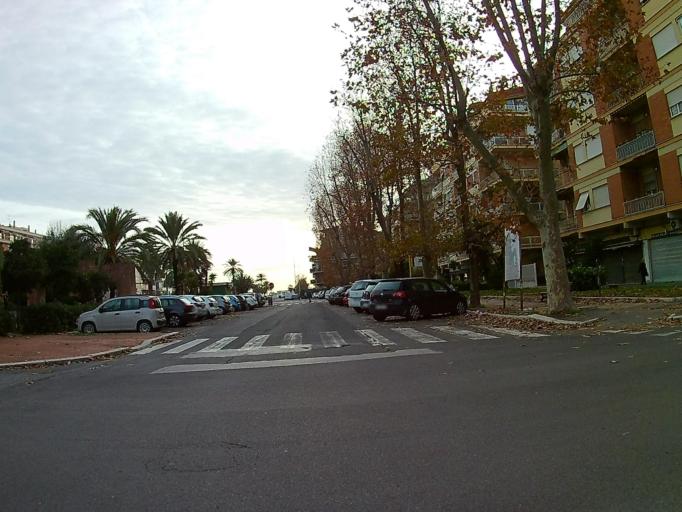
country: IT
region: Latium
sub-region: Citta metropolitana di Roma Capitale
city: Lido di Ostia
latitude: 41.7358
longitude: 12.2686
